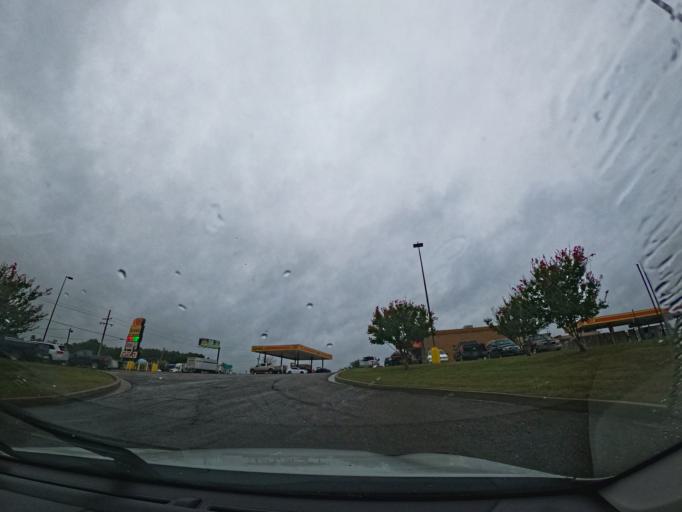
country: US
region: Louisiana
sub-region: Webster Parish
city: Minden
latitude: 32.5826
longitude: -93.2487
